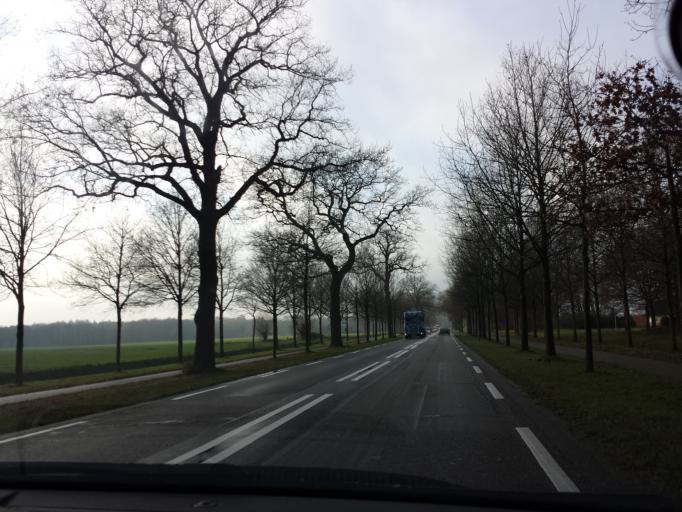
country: NL
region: North Brabant
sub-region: Gemeente Landerd
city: Reek
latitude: 51.7400
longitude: 5.6895
